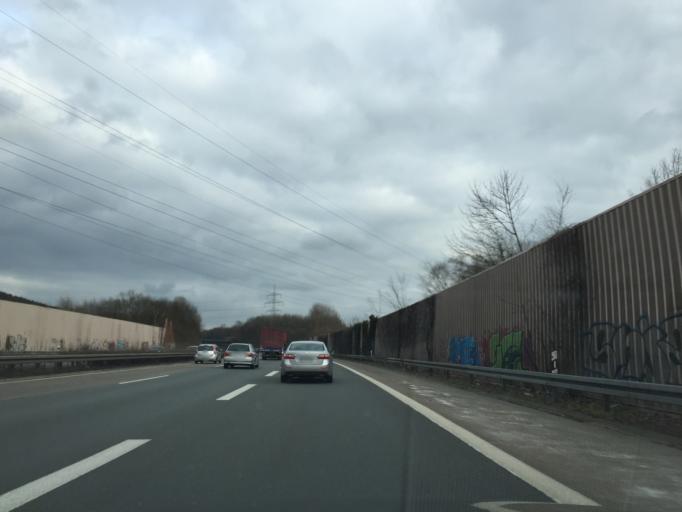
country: DE
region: North Rhine-Westphalia
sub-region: Regierungsbezirk Arnsberg
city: Nachrodt-Wiblingwerde
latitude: 51.3644
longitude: 7.5731
